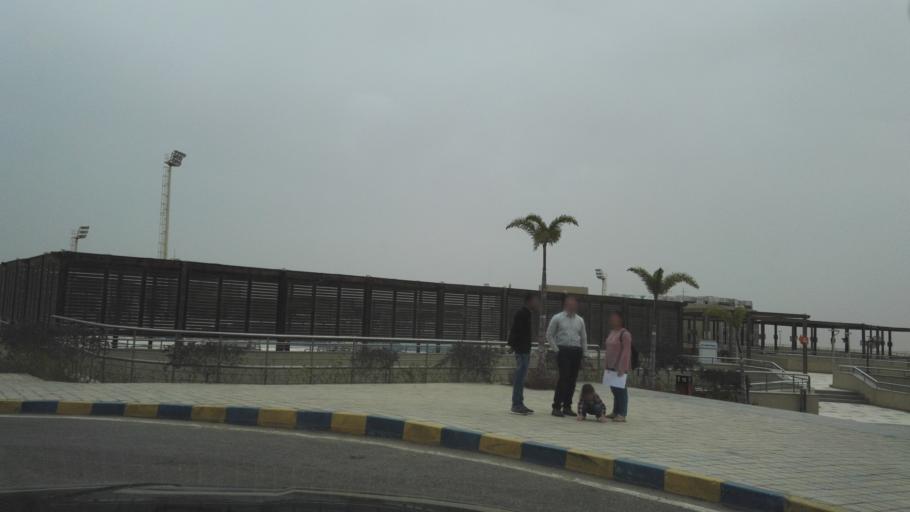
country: EG
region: Muhafazat al Qalyubiyah
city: Al Khankah
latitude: 30.0377
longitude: 31.5274
